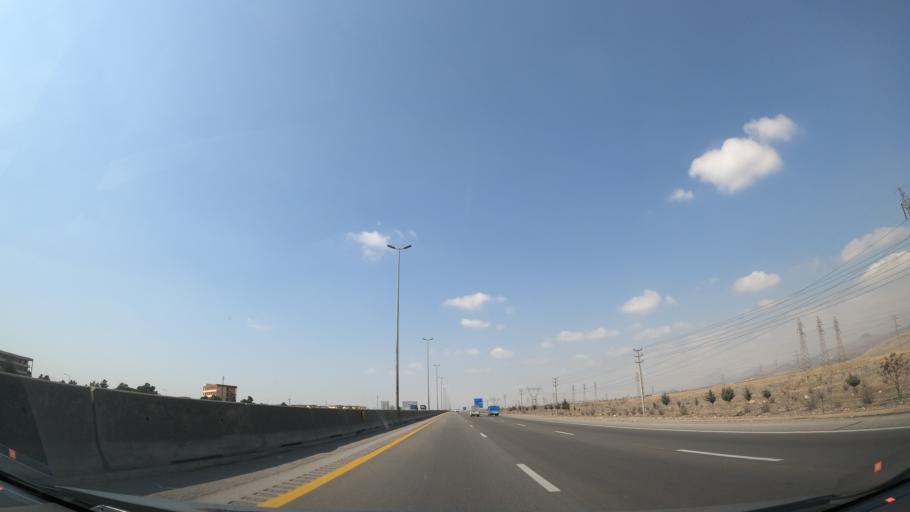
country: IR
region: Qazvin
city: Abyek
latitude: 36.0675
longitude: 50.4847
